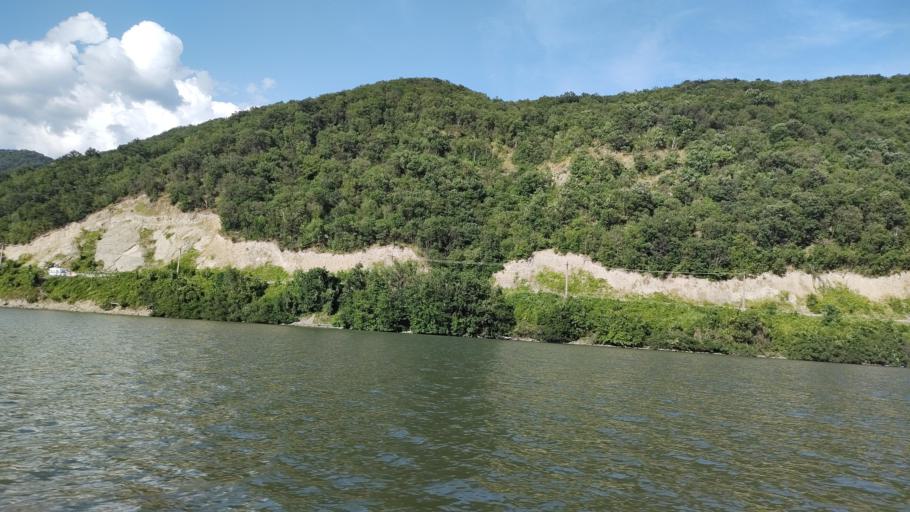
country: RO
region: Mehedinti
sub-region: Comuna Svinita
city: Svinita
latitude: 44.5639
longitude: 22.0304
